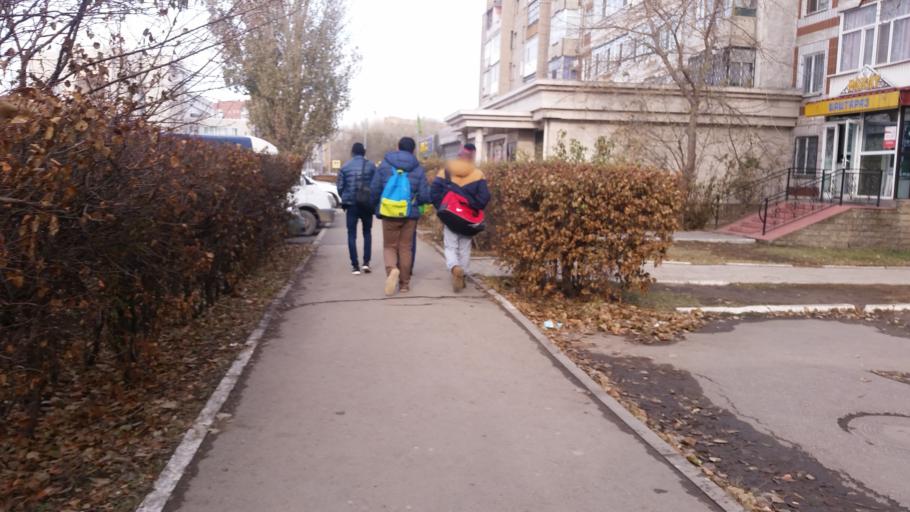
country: KZ
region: Astana Qalasy
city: Astana
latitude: 51.1550
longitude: 71.4742
